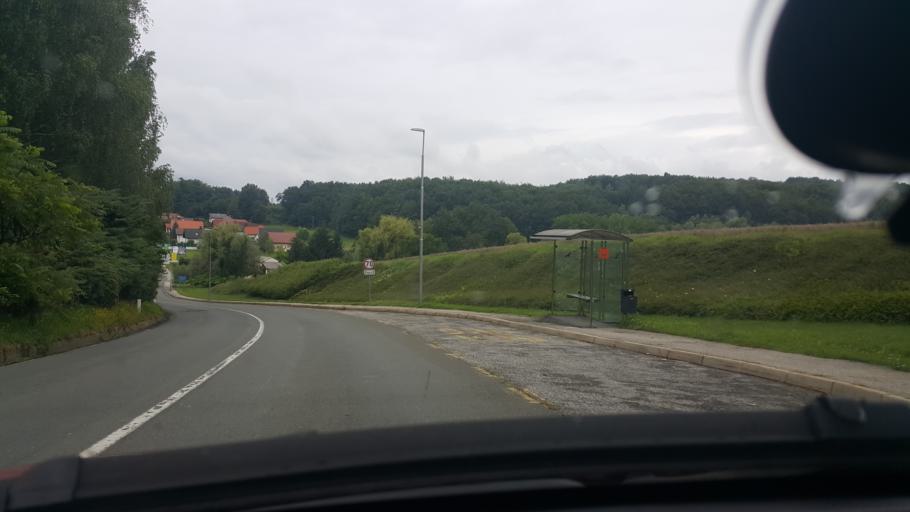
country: SI
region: Ormoz
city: Ormoz
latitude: 46.4075
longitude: 16.1404
